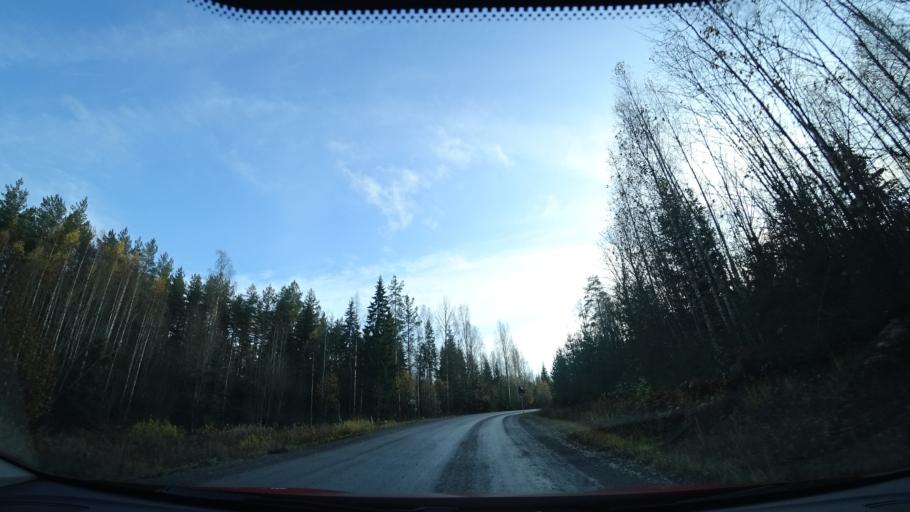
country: FI
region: Uusimaa
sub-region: Helsinki
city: Sibbo
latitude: 60.2955
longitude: 25.2002
